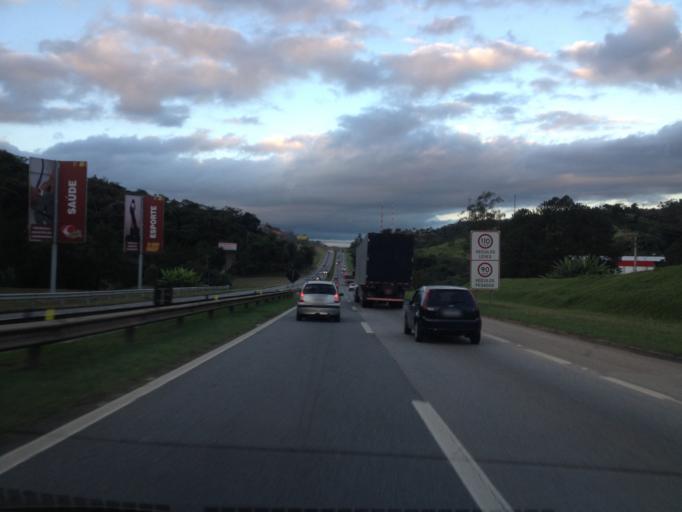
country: BR
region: Sao Paulo
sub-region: Santa Isabel
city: Santa Isabel
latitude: -23.3683
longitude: -46.2338
